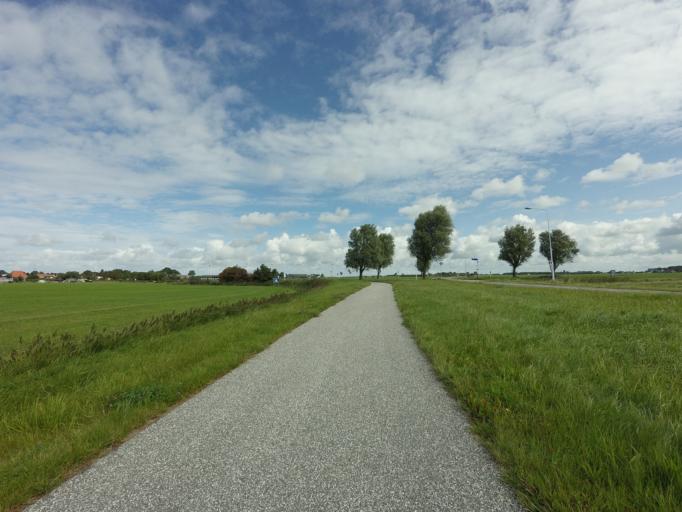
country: NL
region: Friesland
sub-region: Sudwest Fryslan
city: Makkum
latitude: 53.0791
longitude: 5.4268
